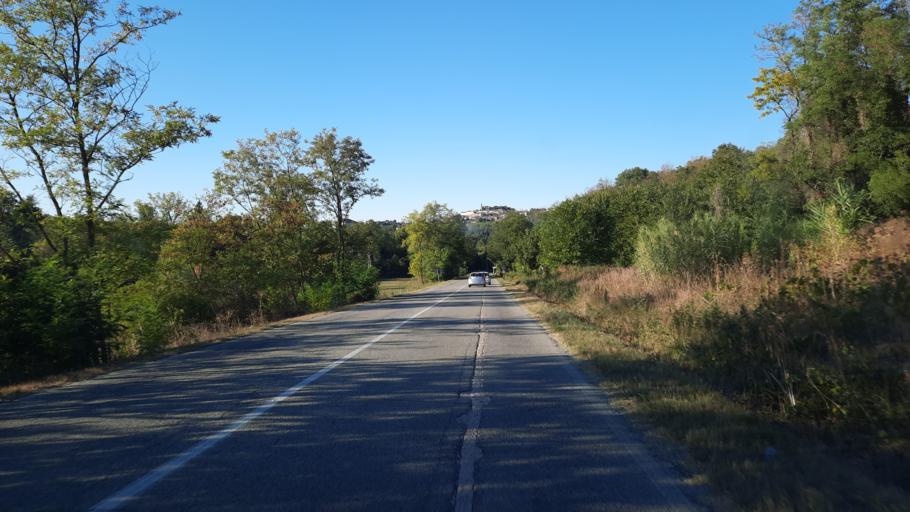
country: IT
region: Piedmont
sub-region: Provincia di Alessandria
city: Vignale Monferrato
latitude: 45.0149
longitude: 8.3887
